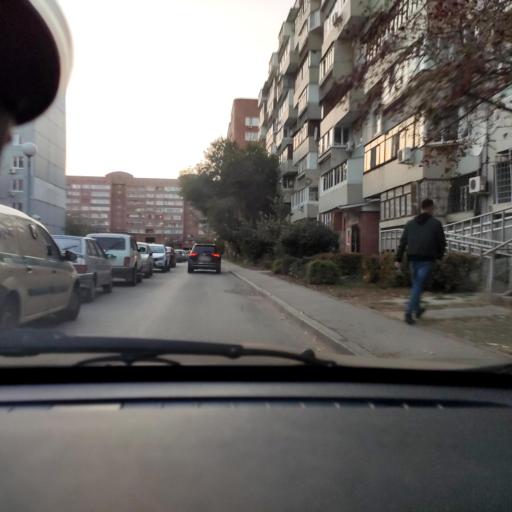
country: RU
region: Samara
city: Tol'yatti
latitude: 53.5437
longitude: 49.3503
